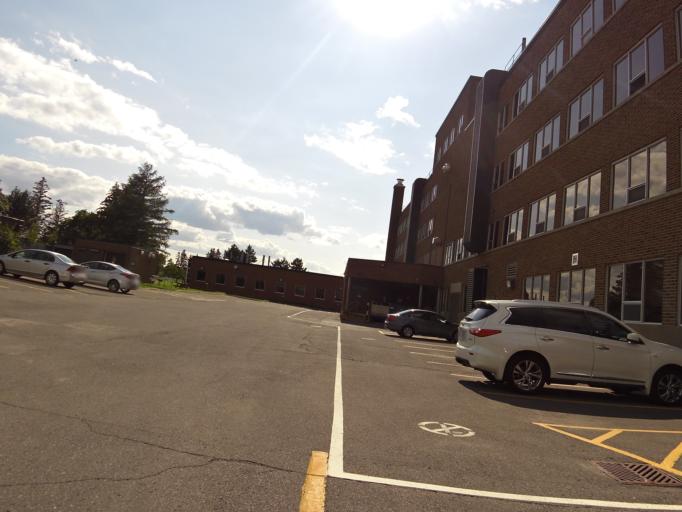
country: CA
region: Ontario
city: Ottawa
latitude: 45.3921
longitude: -75.7180
